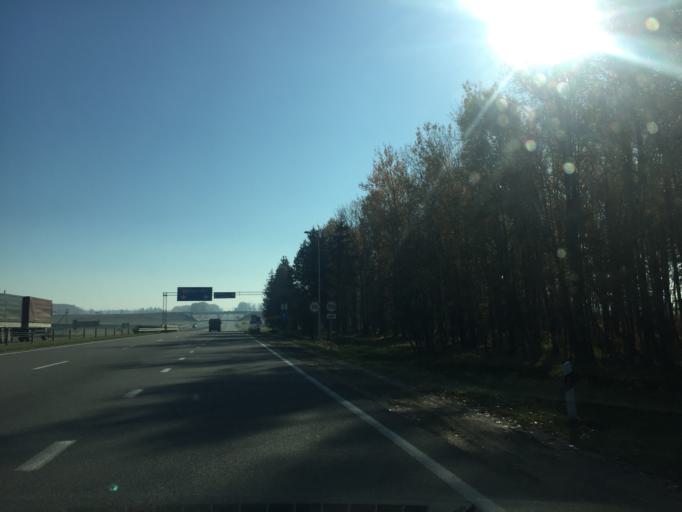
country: BY
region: Mogilev
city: Buynichy
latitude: 53.9518
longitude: 30.2161
